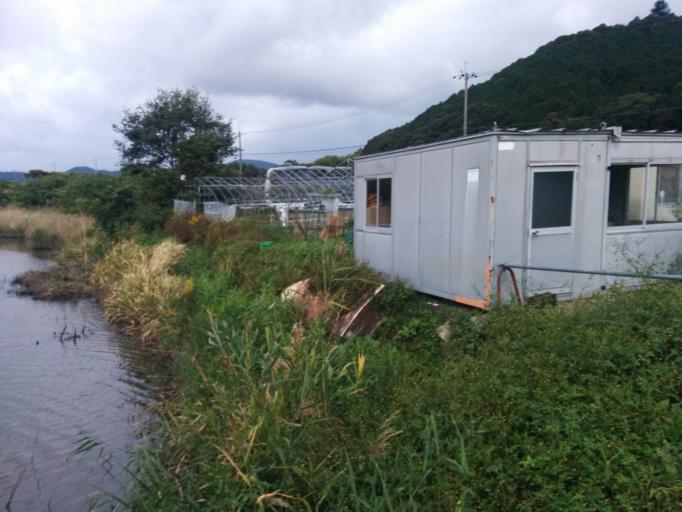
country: JP
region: Shiga Prefecture
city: Omihachiman
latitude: 35.1512
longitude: 136.1400
